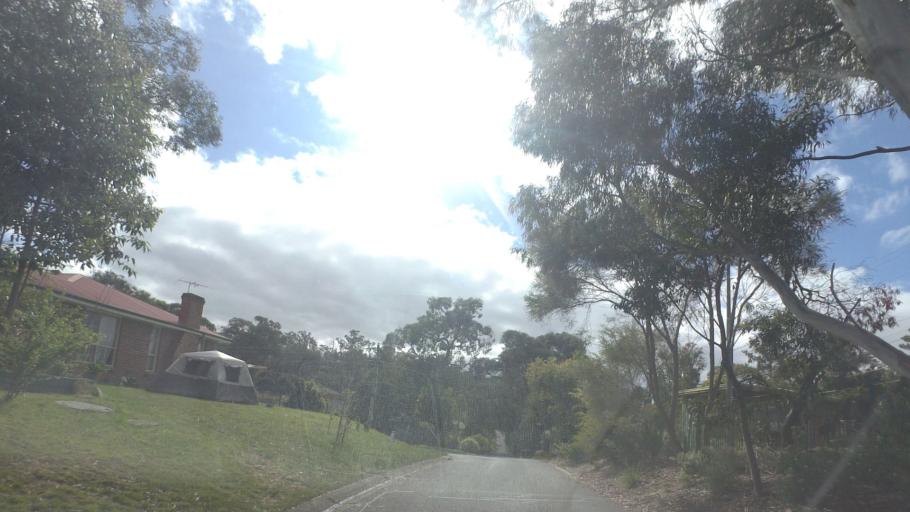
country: AU
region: Victoria
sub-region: Maroondah
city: Croydon South
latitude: -37.8079
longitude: 145.2625
